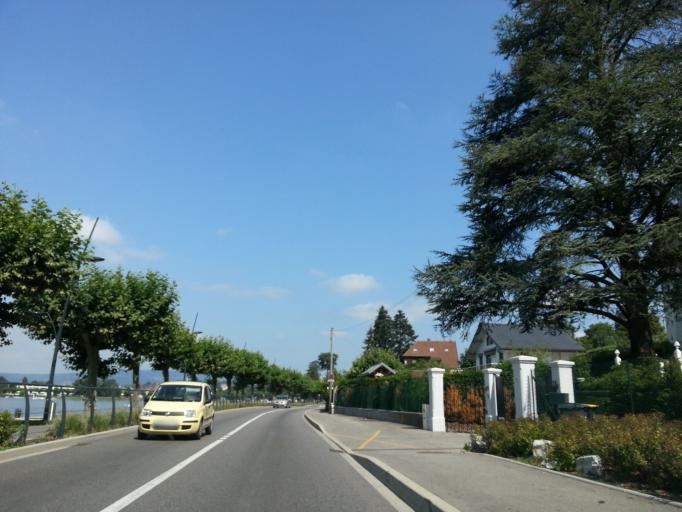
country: FR
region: Rhone-Alpes
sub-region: Departement de la Haute-Savoie
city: Annecy-le-Vieux
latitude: 45.9014
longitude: 6.1610
